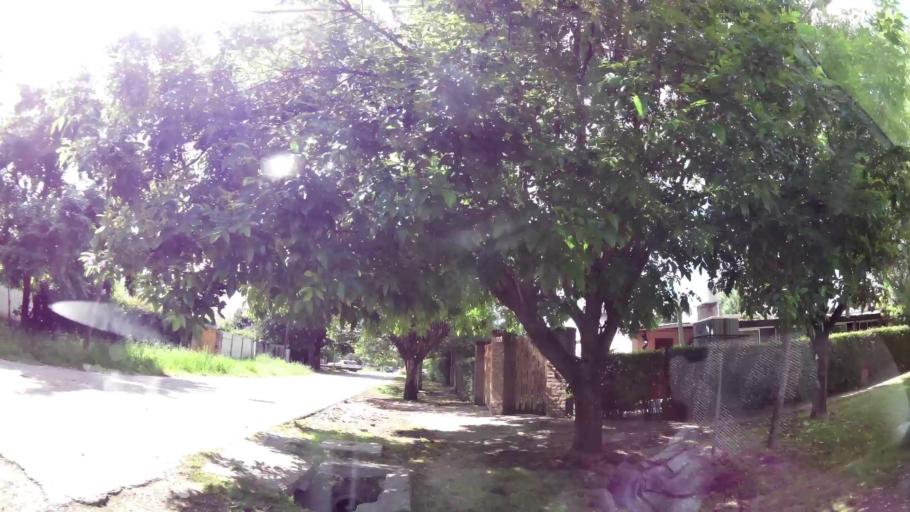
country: AR
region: Buenos Aires
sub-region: Partido de Quilmes
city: Quilmes
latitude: -34.8345
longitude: -58.1714
